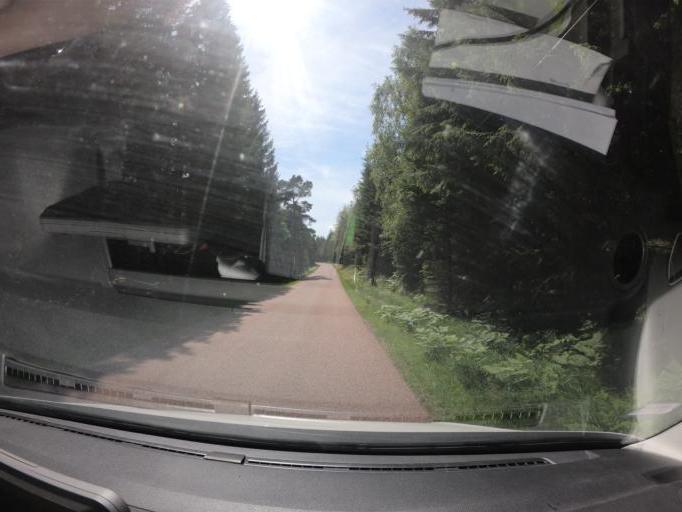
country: SE
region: Skane
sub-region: Orkelljunga Kommun
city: OErkelljunga
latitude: 56.3471
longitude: 13.2874
